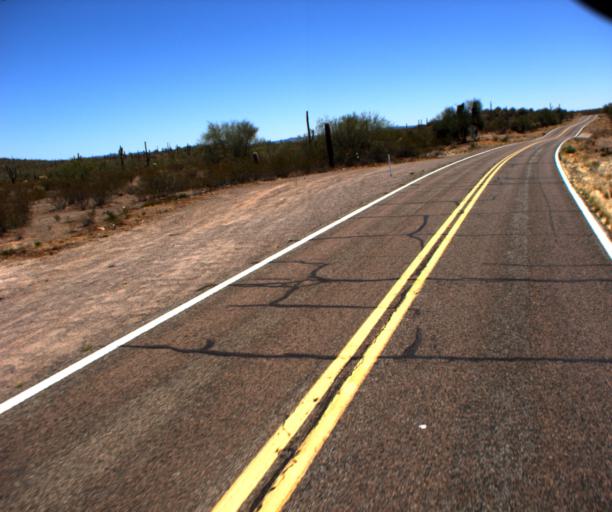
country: US
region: Arizona
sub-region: Pima County
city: Ajo
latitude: 32.2227
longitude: -112.6848
